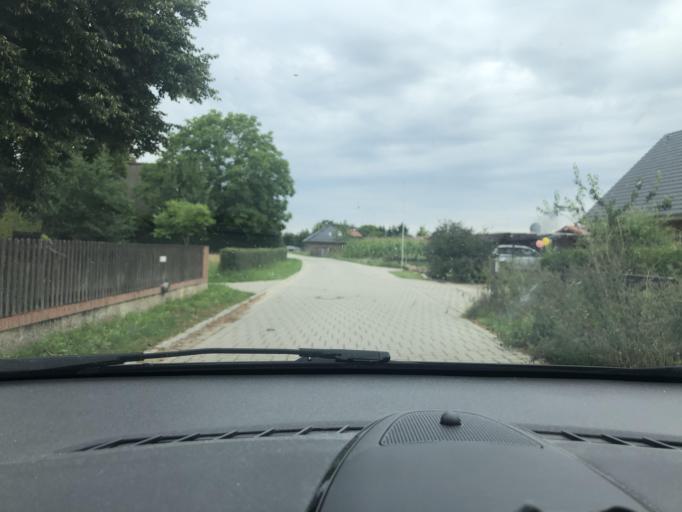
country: DE
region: Mecklenburg-Vorpommern
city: Nostorf
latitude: 53.3531
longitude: 10.6669
